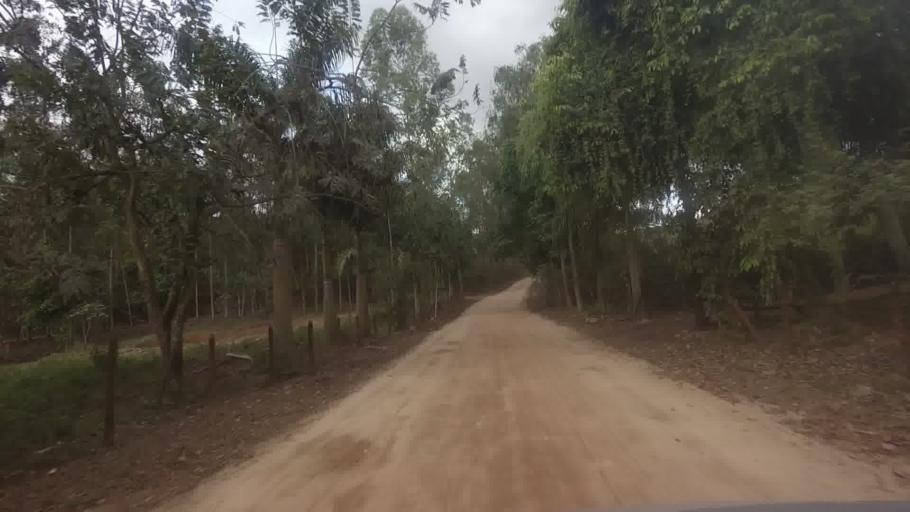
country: BR
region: Espirito Santo
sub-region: Mimoso Do Sul
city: Mimoso do Sul
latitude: -20.9504
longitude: -41.4205
